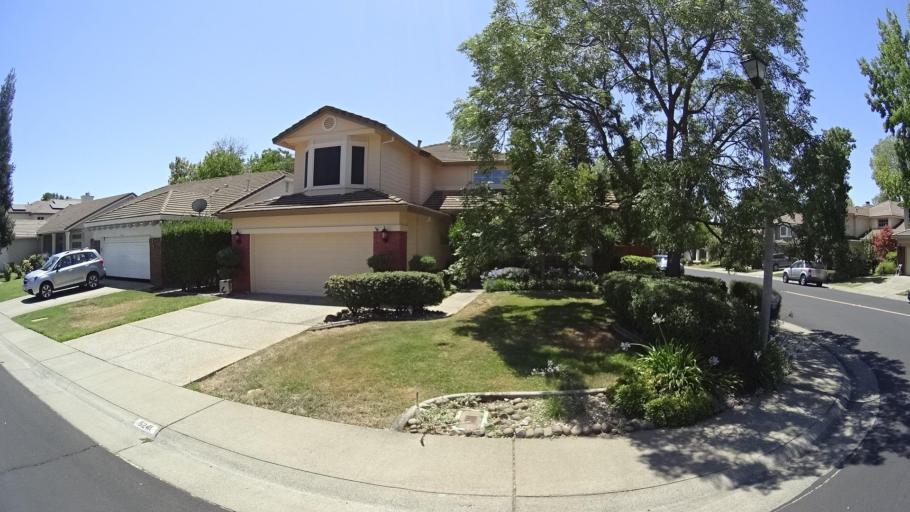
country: US
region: California
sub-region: Placer County
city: Rocklin
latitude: 38.8242
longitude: -121.2643
